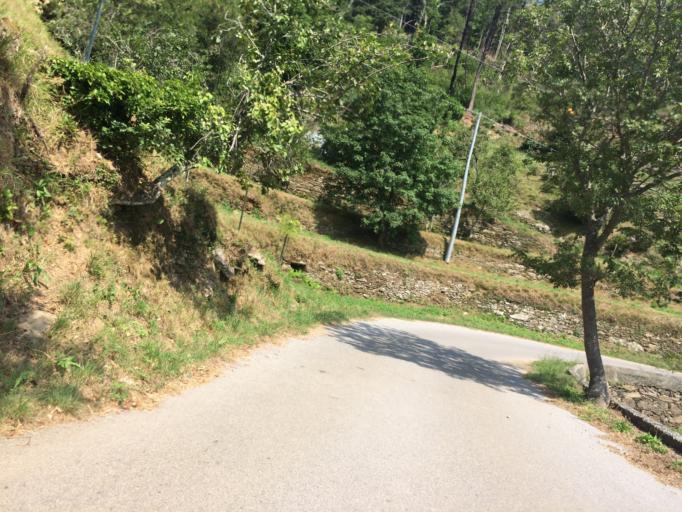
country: IT
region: Liguria
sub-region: Provincia di Savona
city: Varazze
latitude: 44.3973
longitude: 8.5741
